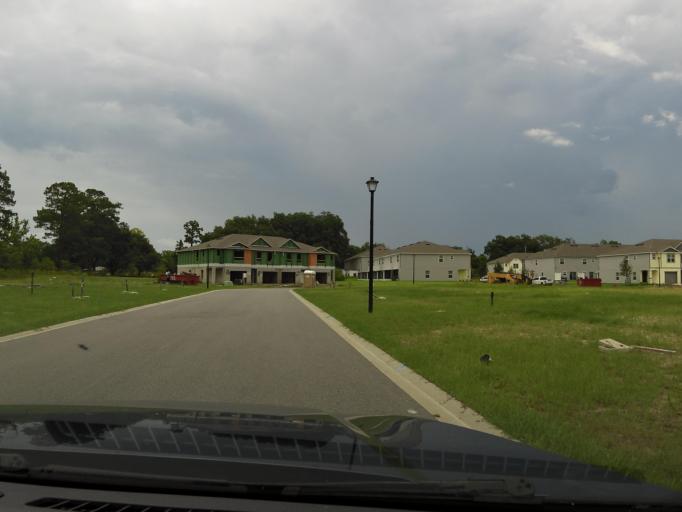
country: US
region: Florida
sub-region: Duval County
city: Jacksonville
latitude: 30.4262
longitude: -81.7004
